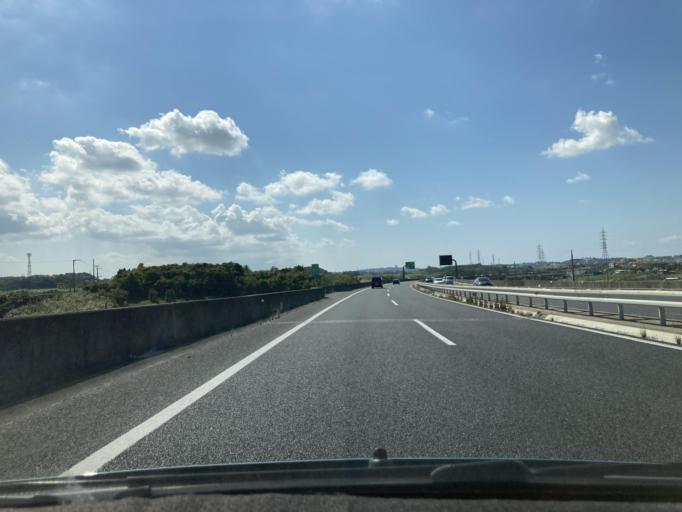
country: JP
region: Okinawa
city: Tomigusuku
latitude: 26.1877
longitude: 127.7377
